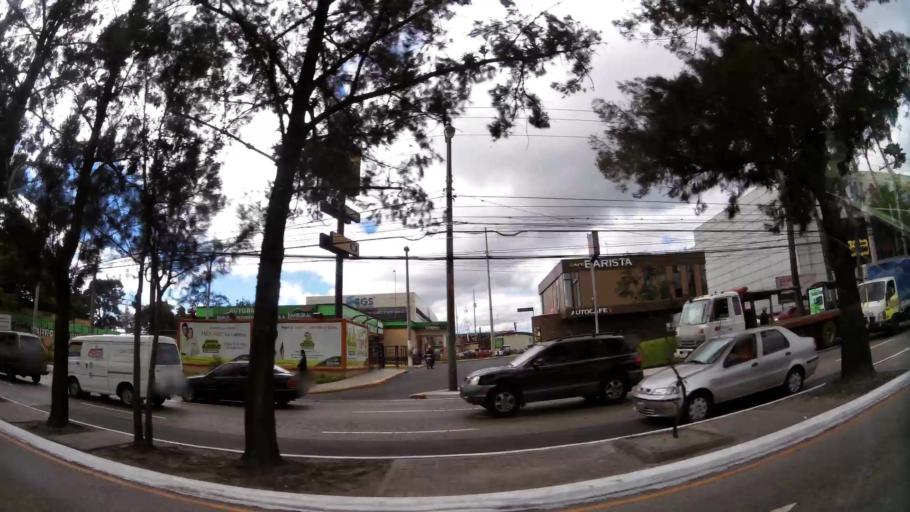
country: GT
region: Guatemala
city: Guatemala City
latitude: 14.6252
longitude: -90.5504
